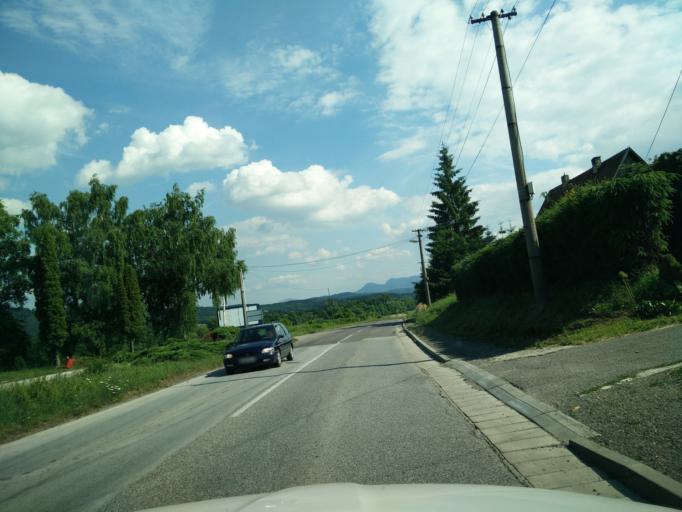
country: SK
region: Nitriansky
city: Prievidza
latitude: 48.8648
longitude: 18.6401
